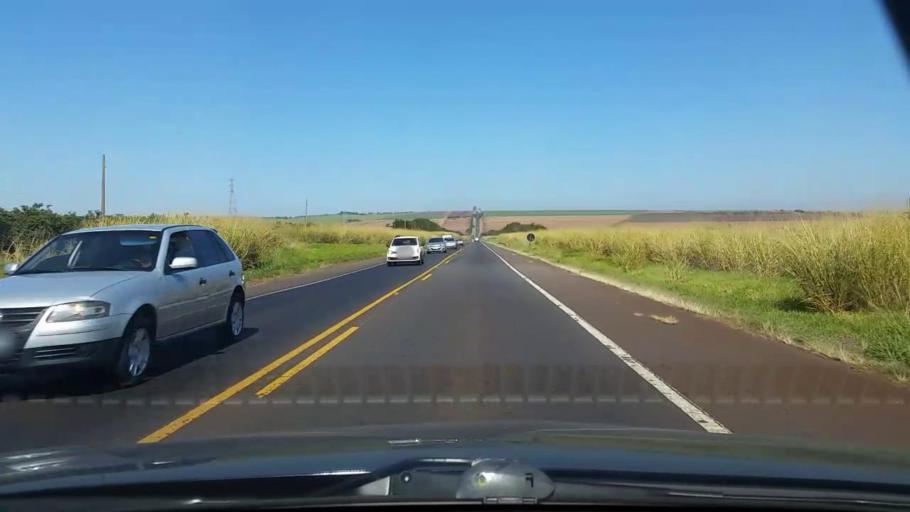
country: BR
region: Sao Paulo
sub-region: Jau
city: Jau
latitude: -22.3594
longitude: -48.5722
